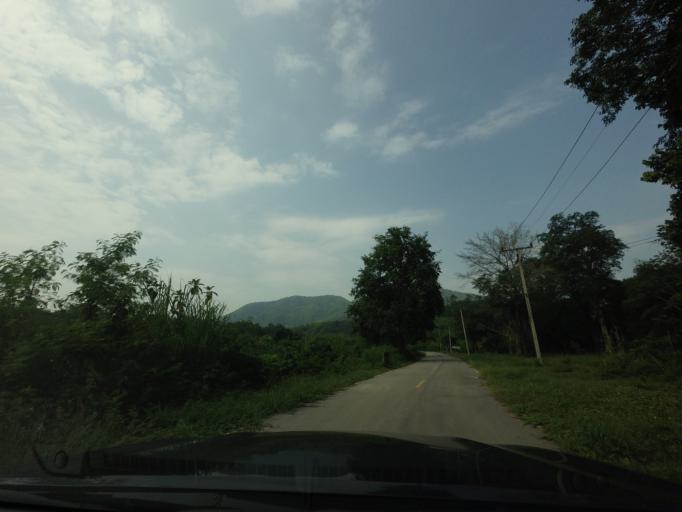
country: TH
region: Loei
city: Chiang Khan
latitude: 17.8136
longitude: 101.5546
